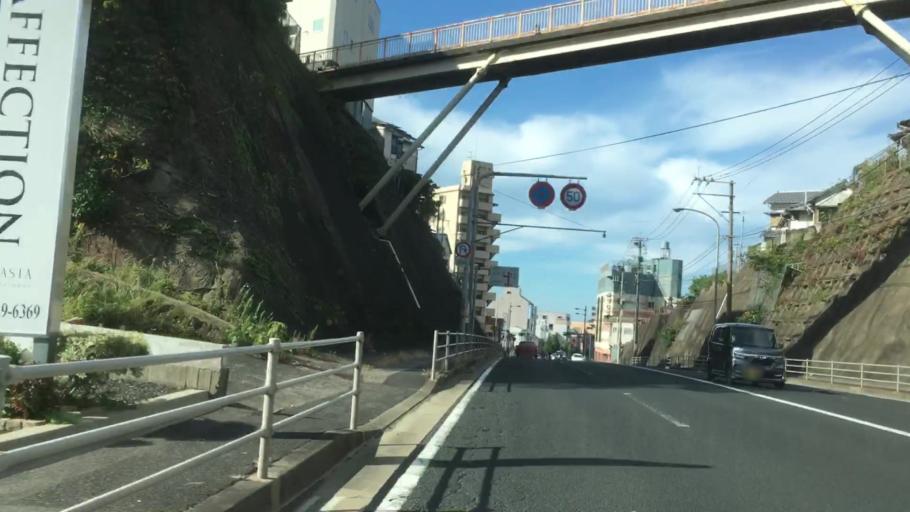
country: JP
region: Nagasaki
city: Sasebo
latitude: 33.1600
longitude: 129.7416
